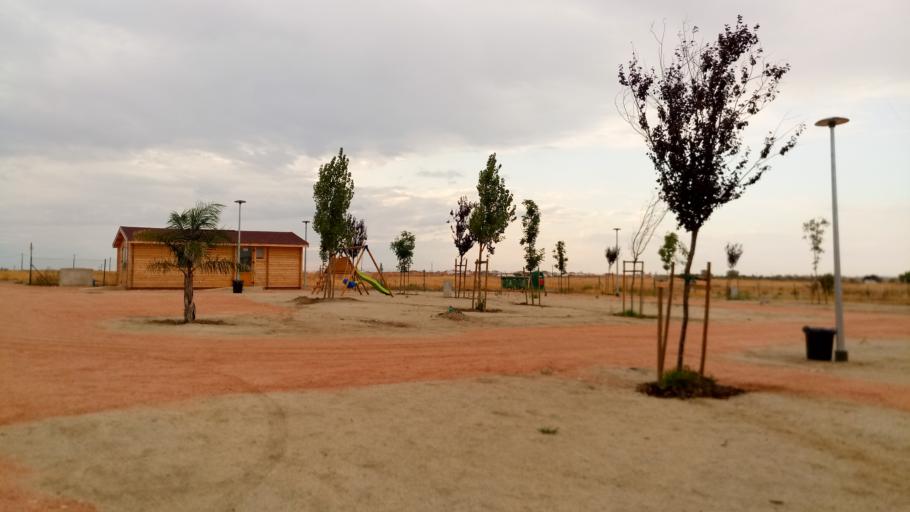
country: PT
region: Evora
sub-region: Reguengos de Monsaraz
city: Reguengos de Monsaraz
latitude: 38.3580
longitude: -7.4645
